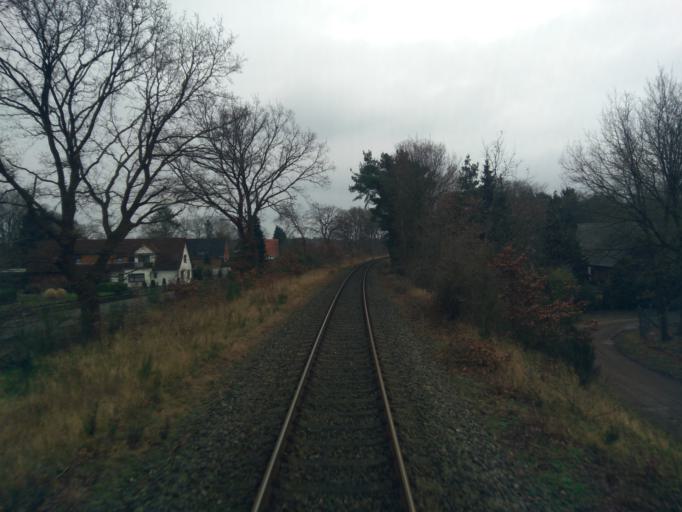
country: DE
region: Lower Saxony
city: Langwedel
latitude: 52.9718
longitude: 9.2175
